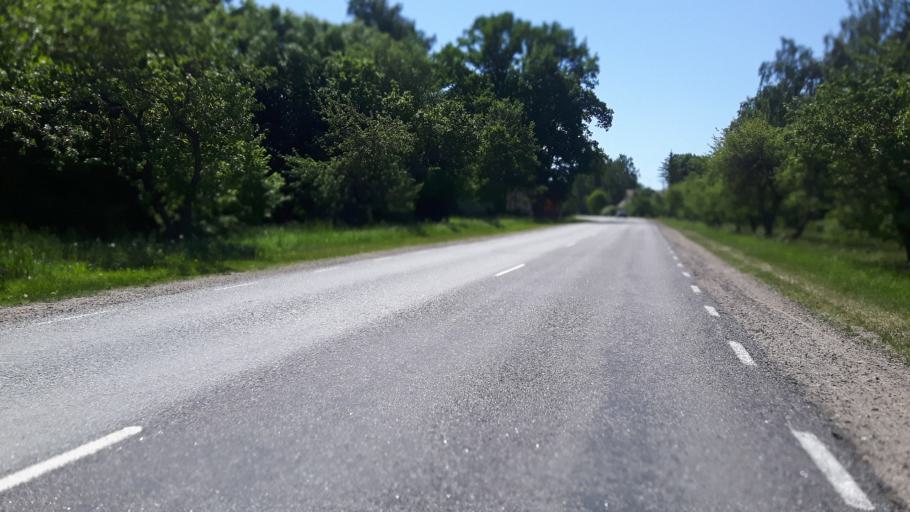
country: EE
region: Paernumaa
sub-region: Tootsi vald
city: Tootsi
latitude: 58.4696
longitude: 24.7917
